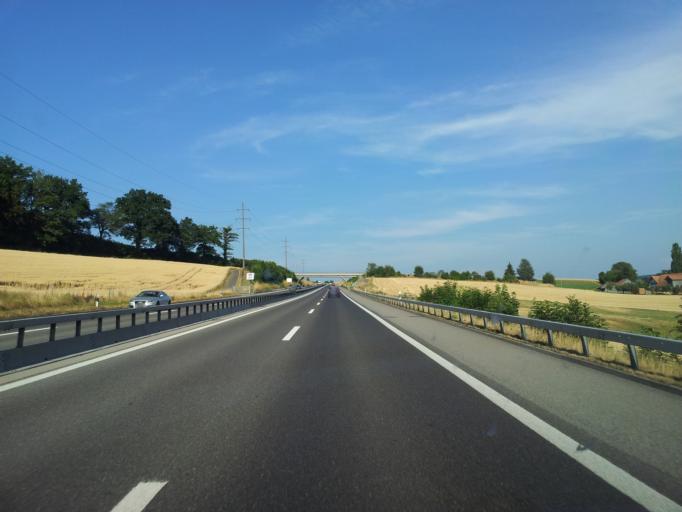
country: CH
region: Fribourg
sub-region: Sense District
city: Schmitten
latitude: 46.8706
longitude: 7.2368
